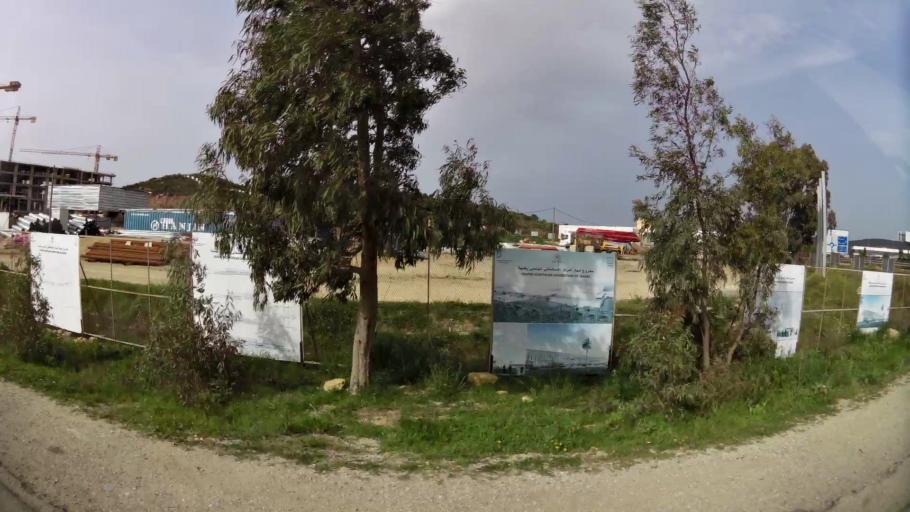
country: MA
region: Tanger-Tetouan
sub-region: Tanger-Assilah
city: Boukhalef
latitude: 35.6817
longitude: -5.9247
